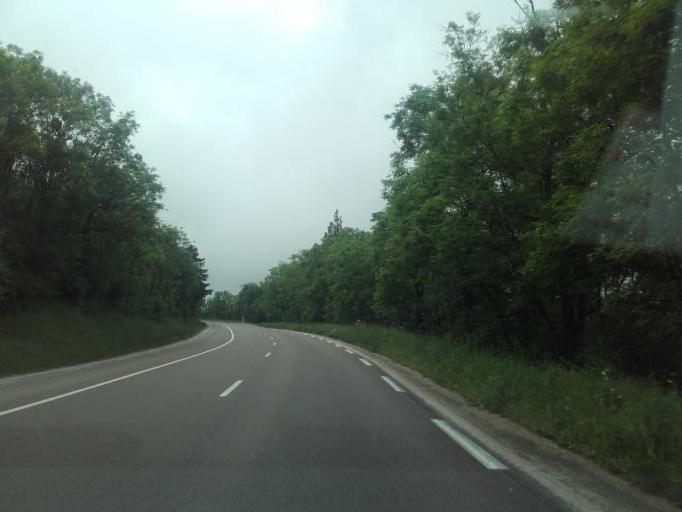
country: FR
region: Bourgogne
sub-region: Departement de la Cote-d'Or
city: Nolay
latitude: 46.9663
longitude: 4.6778
